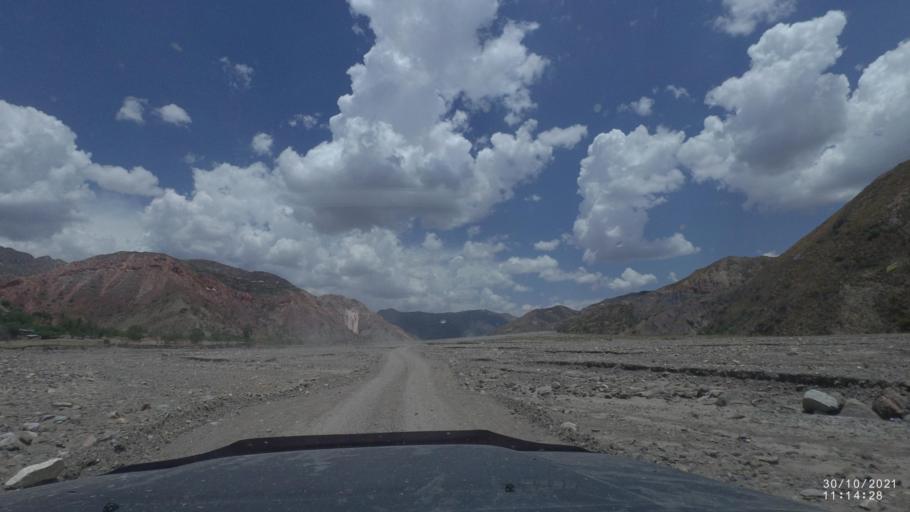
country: BO
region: Cochabamba
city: Sipe Sipe
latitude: -17.5265
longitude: -66.5830
